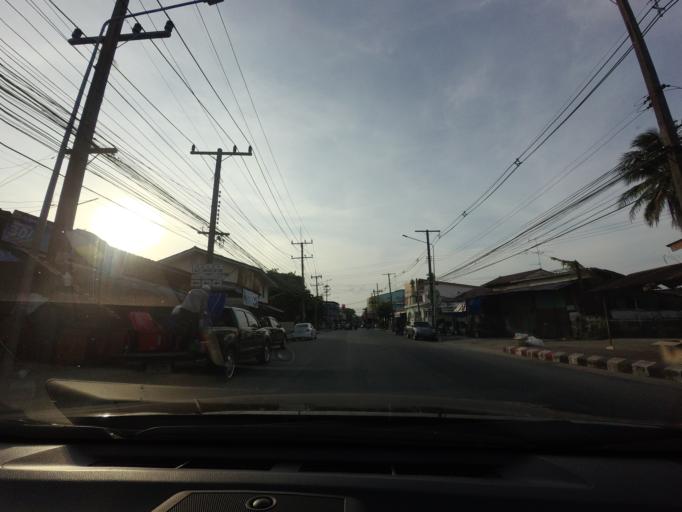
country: TH
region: Narathiwat
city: Narathiwat
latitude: 6.4239
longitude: 101.8282
